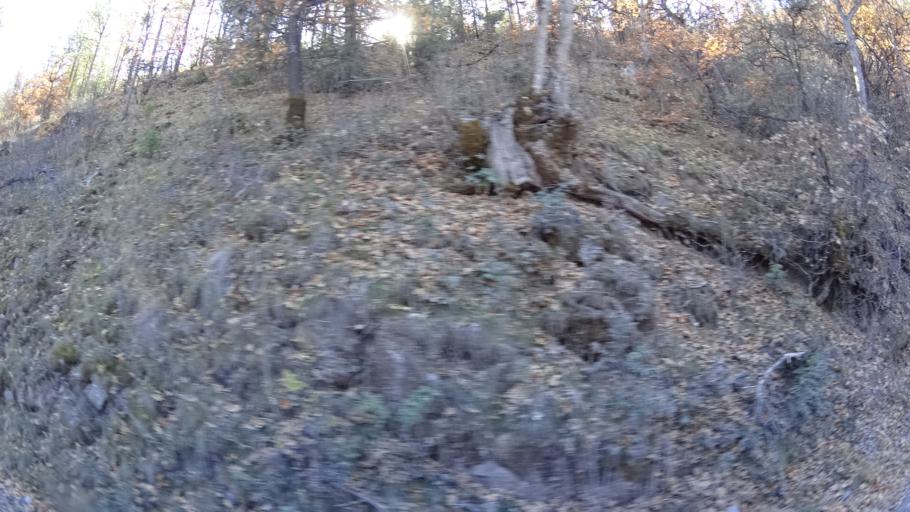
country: US
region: California
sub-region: Siskiyou County
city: Yreka
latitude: 41.8249
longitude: -122.6586
